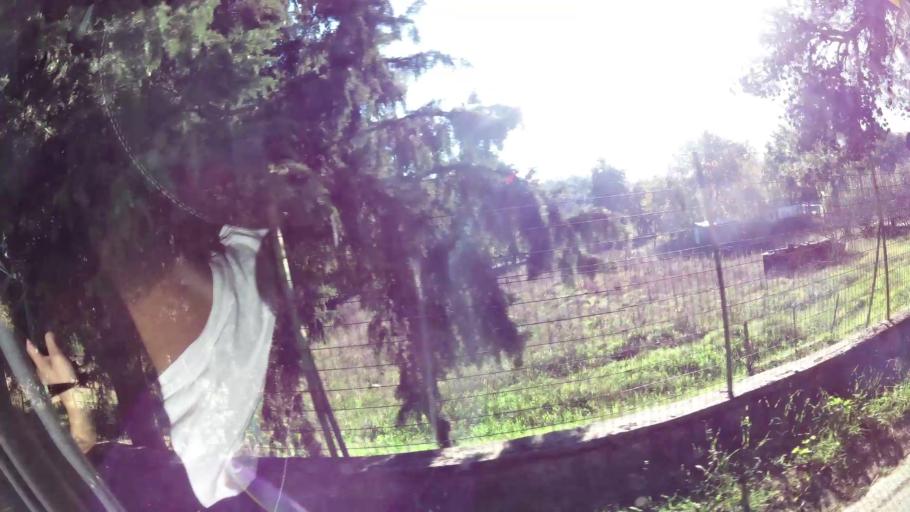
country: GR
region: Attica
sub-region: Nomarchia Anatolikis Attikis
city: Stamata
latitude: 38.1303
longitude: 23.8795
